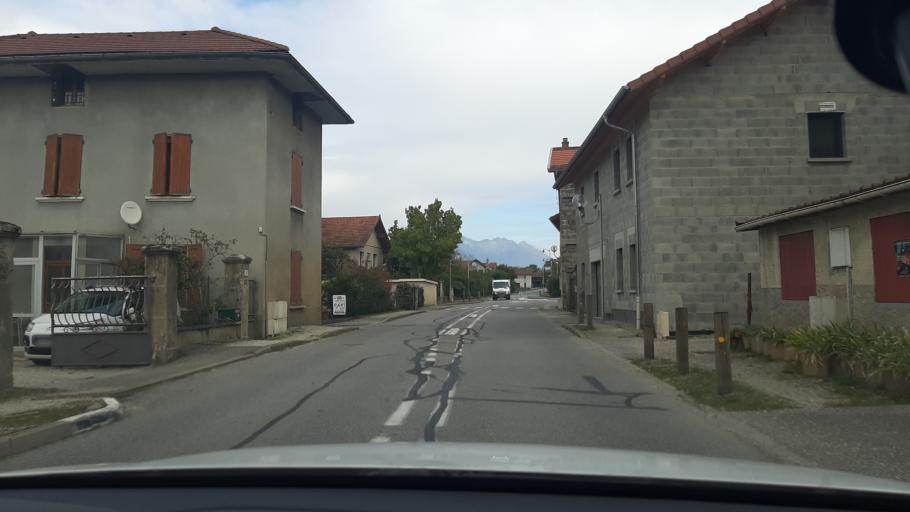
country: FR
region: Rhone-Alpes
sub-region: Departement de l'Isere
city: Pontcharra
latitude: 45.4482
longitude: 6.0384
